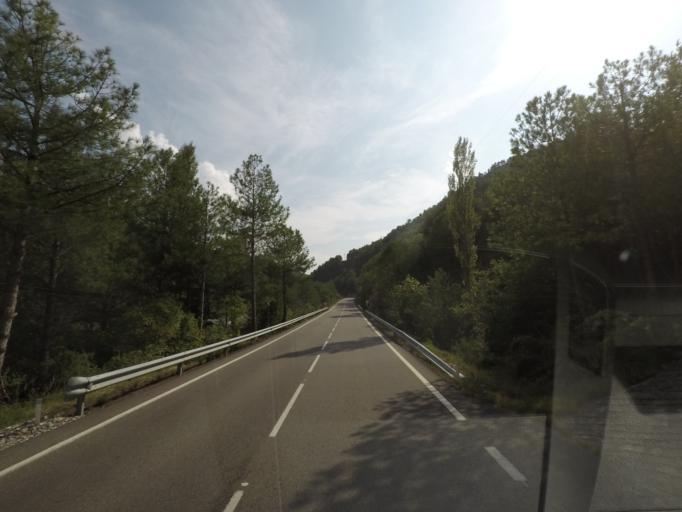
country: ES
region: Aragon
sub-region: Provincia de Huesca
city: Puertolas
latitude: 42.5413
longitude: 0.1586
